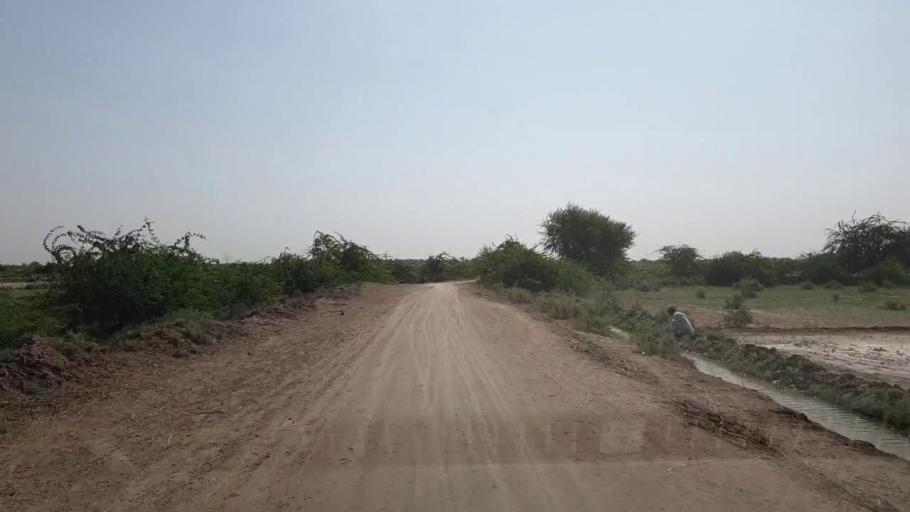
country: PK
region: Sindh
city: Tando Bago
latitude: 24.7375
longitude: 69.0219
